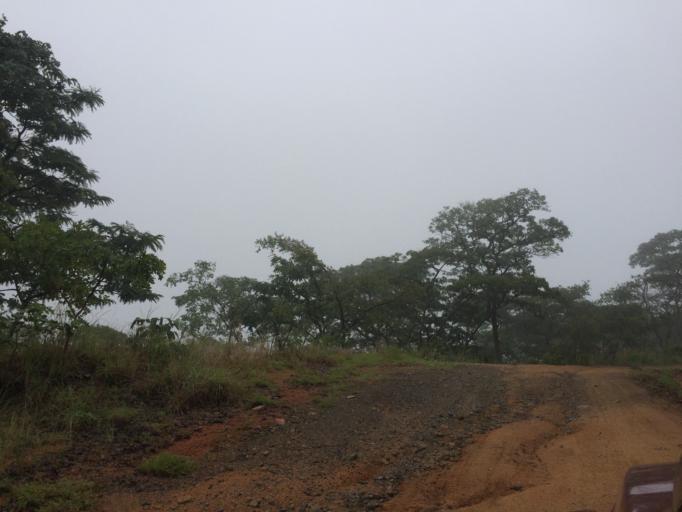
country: TZ
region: Mbeya
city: Chimala
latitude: -8.8695
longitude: 33.9928
